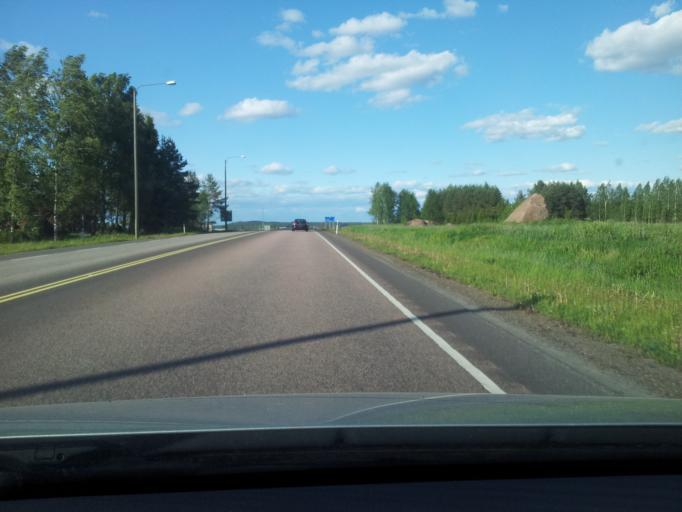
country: FI
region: Kymenlaakso
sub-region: Kouvola
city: Elimaeki
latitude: 60.7346
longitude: 26.4378
